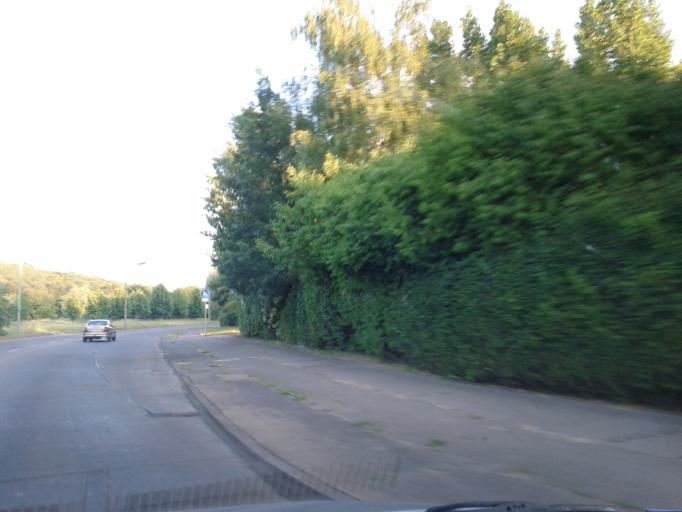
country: DE
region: Berlin
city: Marzahn
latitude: 52.5600
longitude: 13.5751
